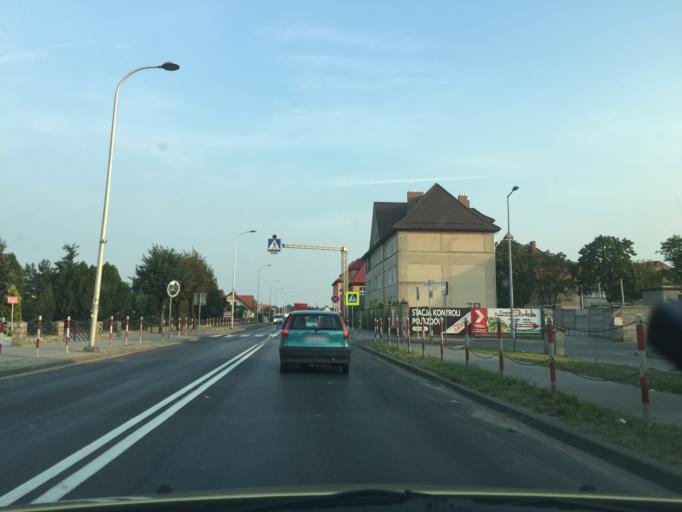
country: PL
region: Greater Poland Voivodeship
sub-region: Powiat jarocinski
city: Jarocin
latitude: 51.9629
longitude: 17.5113
